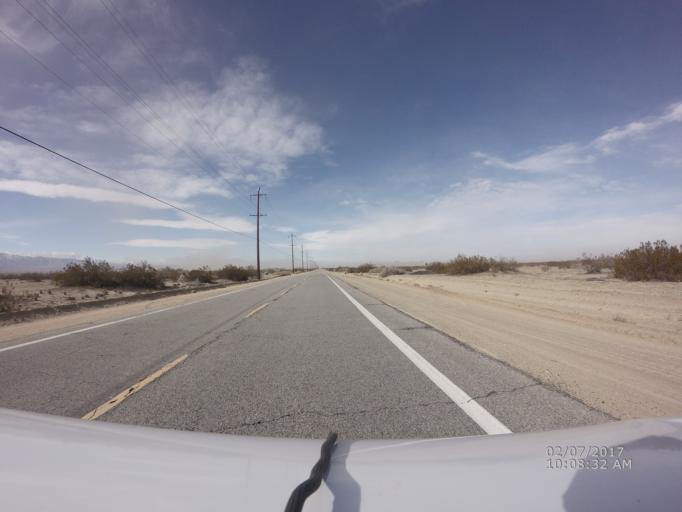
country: US
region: California
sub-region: Los Angeles County
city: Lake Los Angeles
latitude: 34.5799
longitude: -117.7549
